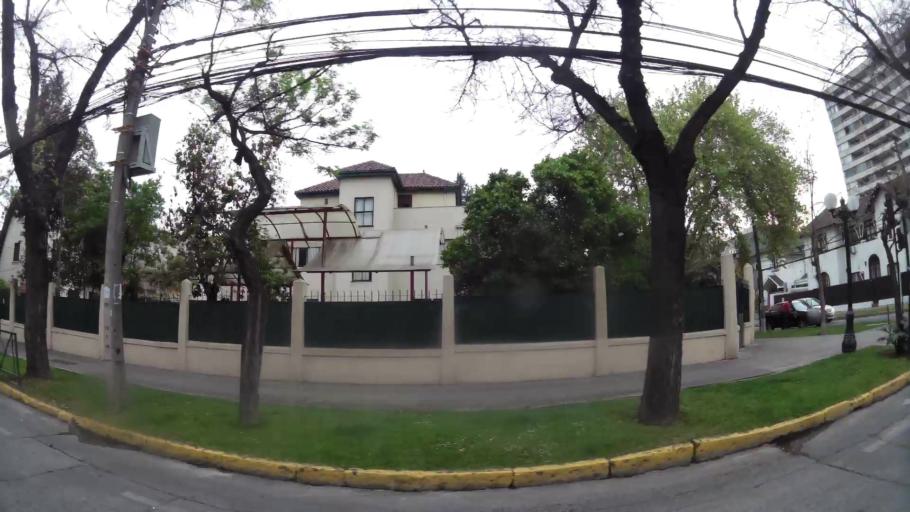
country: CL
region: Santiago Metropolitan
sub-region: Provincia de Santiago
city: Santiago
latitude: -33.4356
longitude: -70.6193
